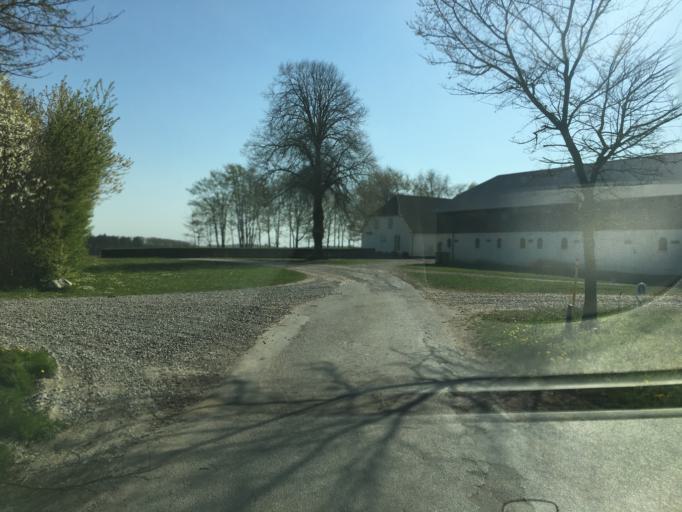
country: DK
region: South Denmark
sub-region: Tonder Kommune
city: Toftlund
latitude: 55.0659
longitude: 9.1483
